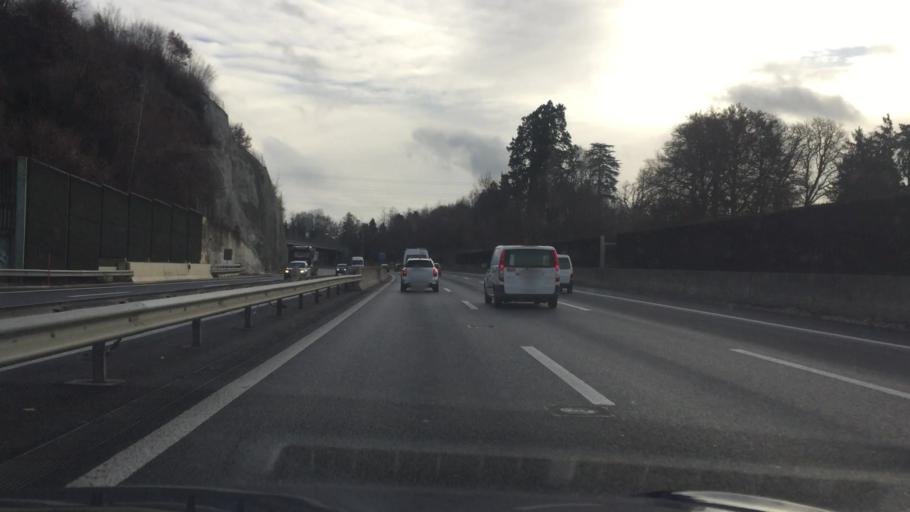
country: CH
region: Vaud
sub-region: Lausanne District
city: Romanel
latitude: 46.5573
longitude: 6.5974
